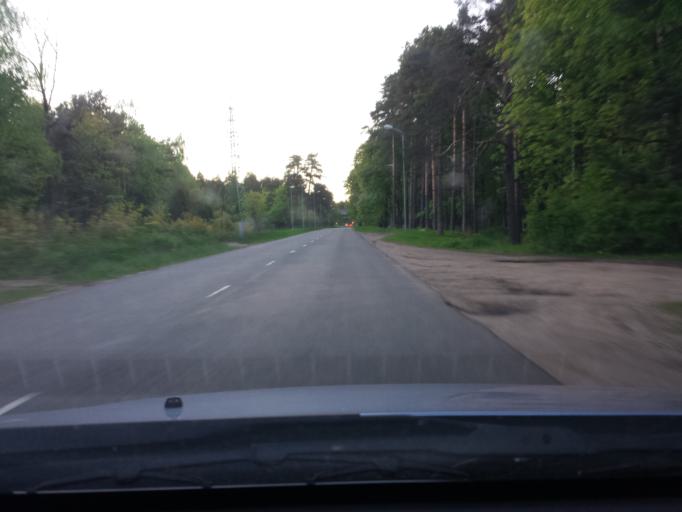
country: LV
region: Riga
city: Riga
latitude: 56.9921
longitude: 24.1406
